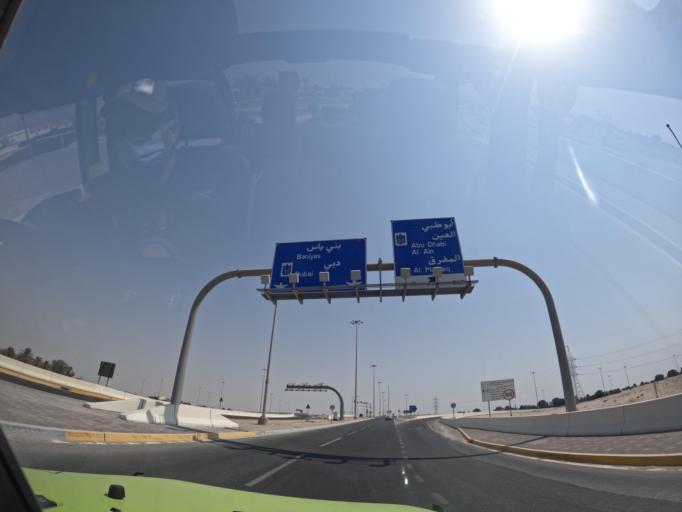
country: AE
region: Abu Dhabi
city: Abu Dhabi
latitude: 24.3291
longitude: 54.6211
